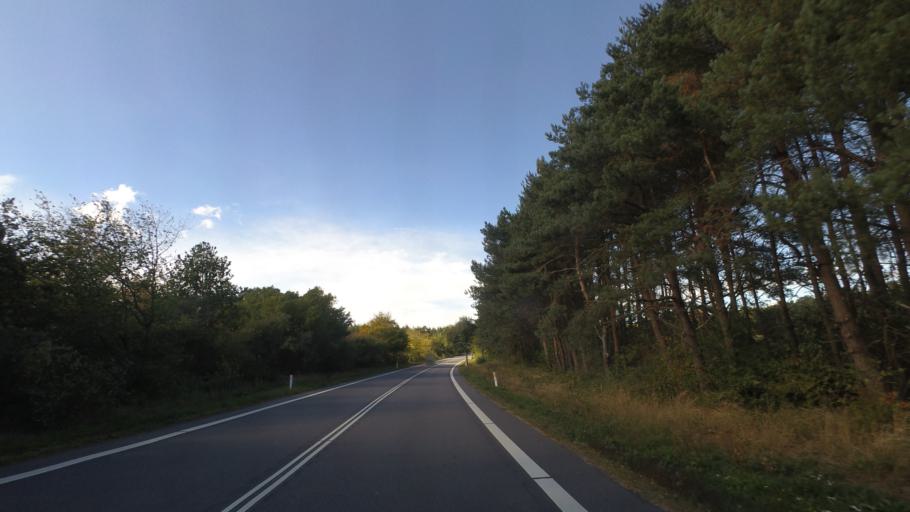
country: DK
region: Capital Region
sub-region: Bornholm Kommune
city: Ronne
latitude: 55.0804
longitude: 14.7559
